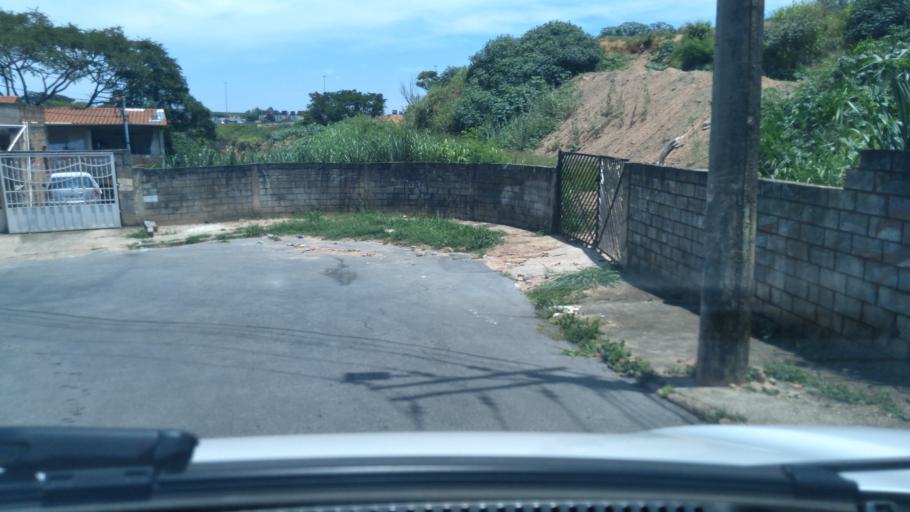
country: BR
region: Minas Gerais
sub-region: Contagem
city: Contagem
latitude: -19.9277
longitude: -44.0099
